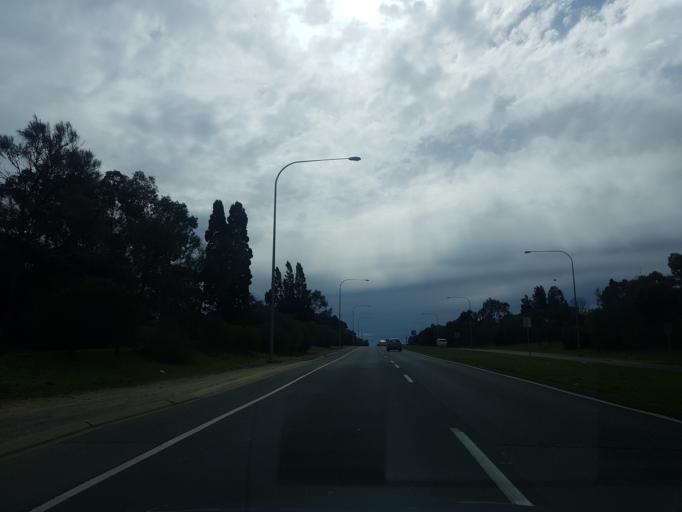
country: AU
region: South Australia
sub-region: Tea Tree Gully
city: Modbury
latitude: -34.8166
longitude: 138.6766
